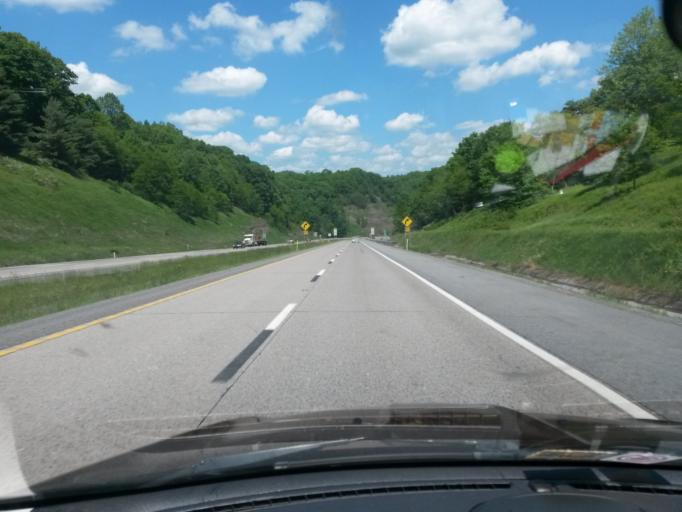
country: US
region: West Virginia
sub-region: Summers County
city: Hinton
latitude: 37.7801
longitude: -80.9708
